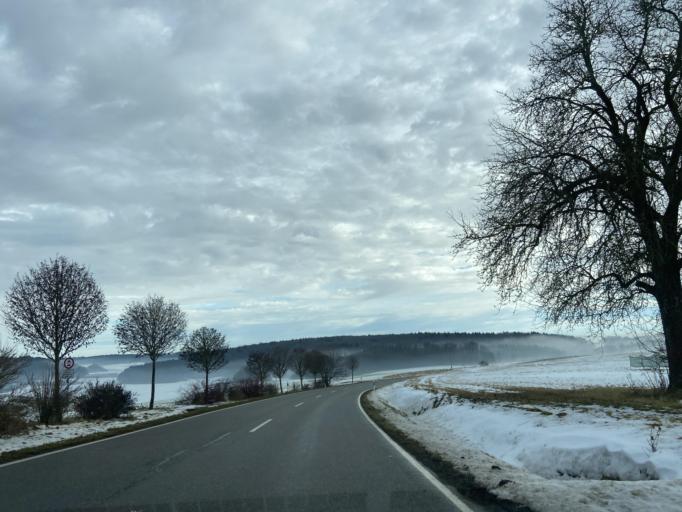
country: DE
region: Baden-Wuerttemberg
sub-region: Tuebingen Region
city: Hettingen
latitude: 48.1840
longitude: 9.2893
